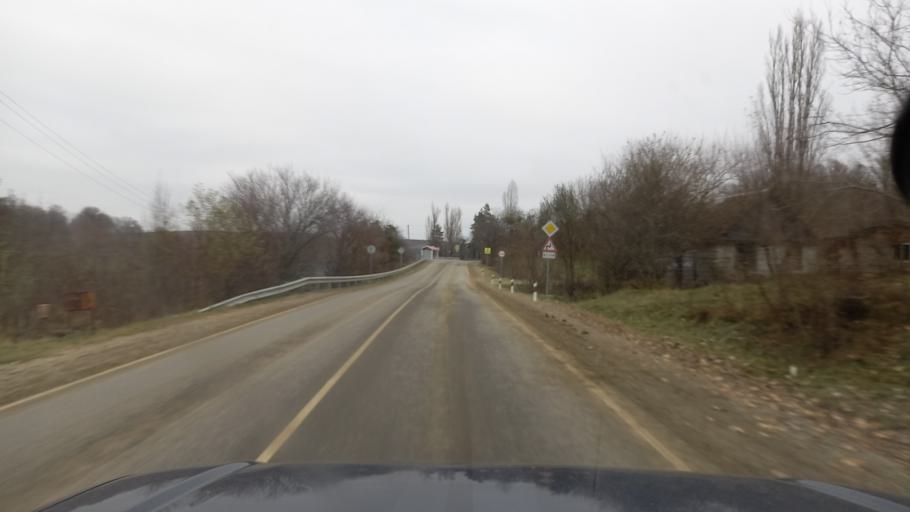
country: RU
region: Krasnodarskiy
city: Saratovskaya
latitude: 44.5461
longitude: 39.2867
